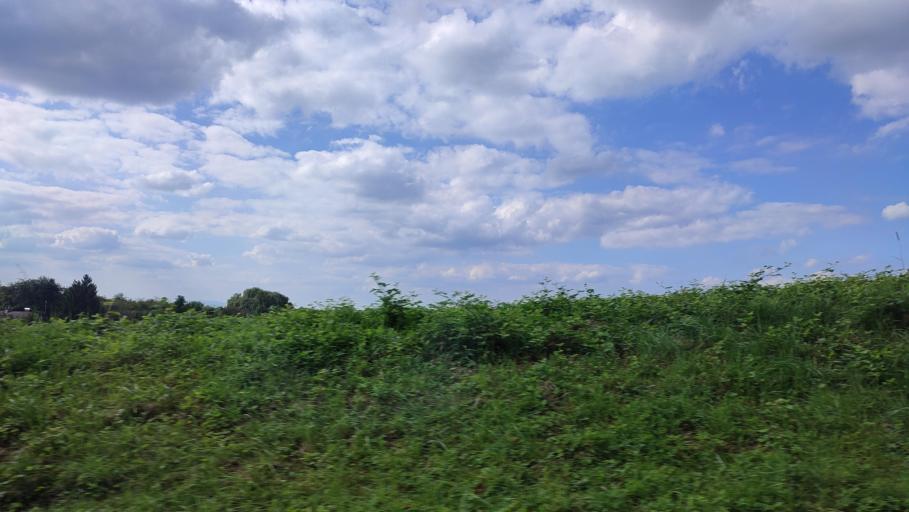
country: DE
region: Baden-Wuerttemberg
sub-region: Freiburg Region
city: Appenweier
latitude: 48.5291
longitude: 8.0161
